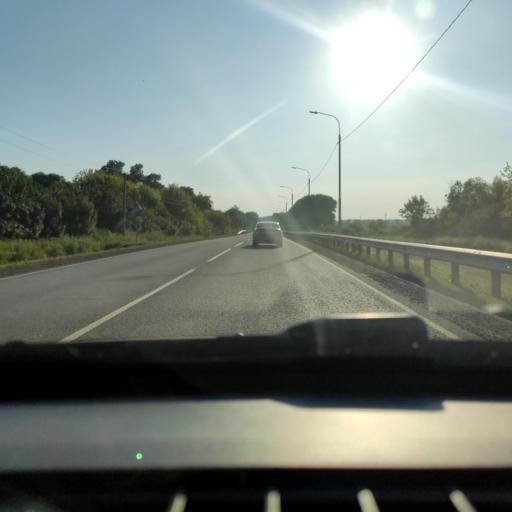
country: RU
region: Voronezj
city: Kashirskoye
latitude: 51.4582
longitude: 39.8089
